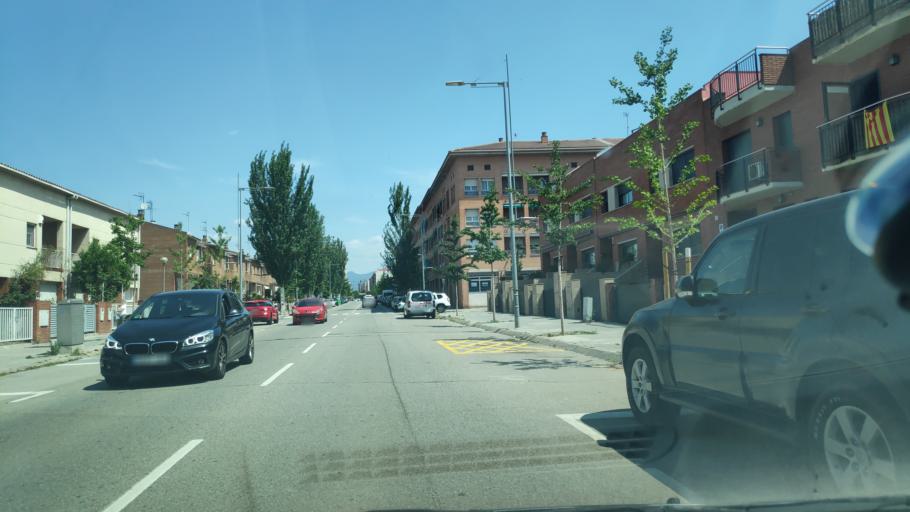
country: ES
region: Catalonia
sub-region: Provincia de Barcelona
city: Granollers
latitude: 41.5986
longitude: 2.2823
